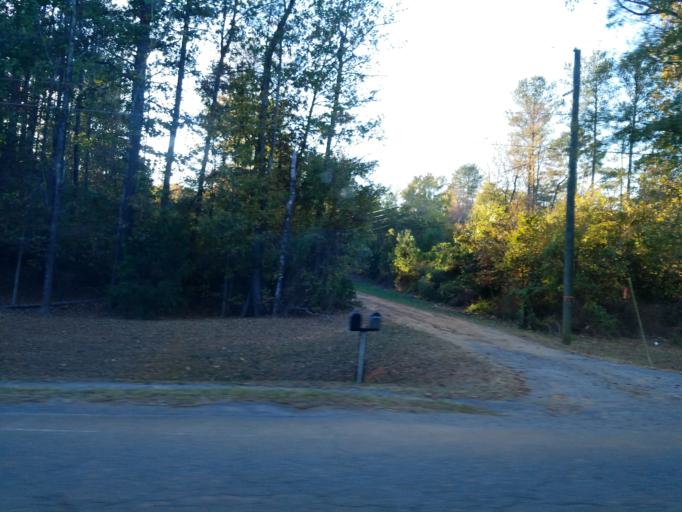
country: US
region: Georgia
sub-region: Bartow County
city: Adairsville
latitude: 34.3051
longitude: -84.9381
